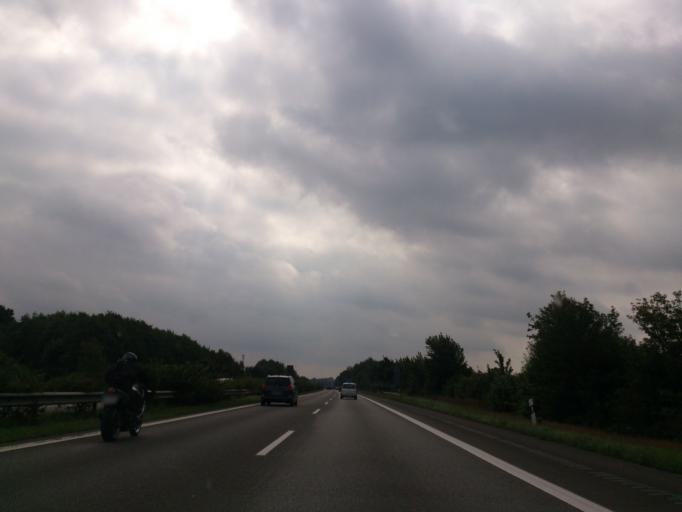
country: DE
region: Schleswig-Holstein
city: Seeth-Ekholt
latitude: 53.7239
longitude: 9.7375
